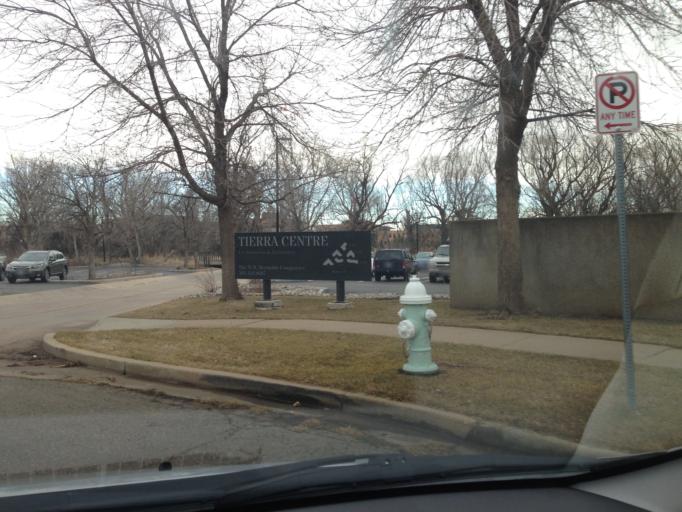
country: US
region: Colorado
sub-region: Boulder County
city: Boulder
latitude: 40.0190
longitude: -105.2396
